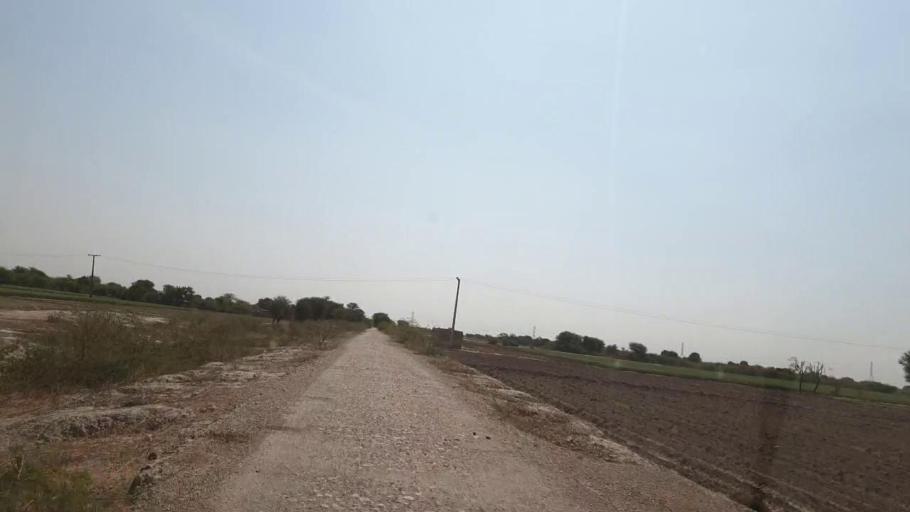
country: PK
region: Sindh
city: Nabisar
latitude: 25.0693
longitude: 69.5527
